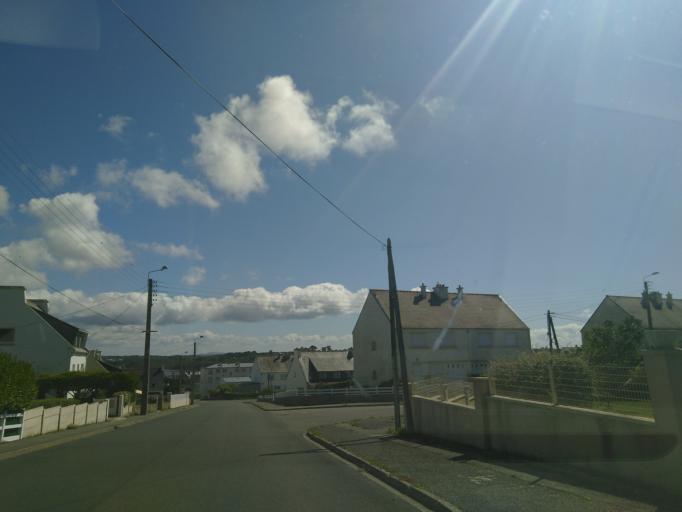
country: FR
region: Brittany
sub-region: Departement du Finistere
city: Camaret-sur-Mer
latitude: 48.2797
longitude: -4.6058
